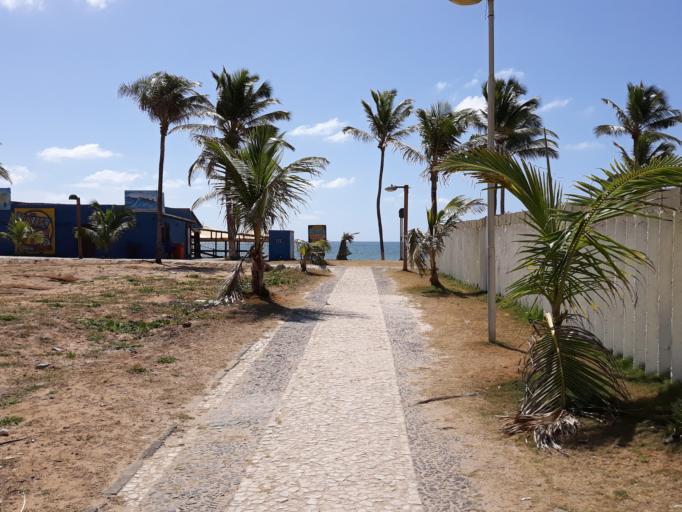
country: BR
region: Bahia
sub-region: Lauro De Freitas
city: Lauro de Freitas
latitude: -12.8900
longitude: -38.2889
